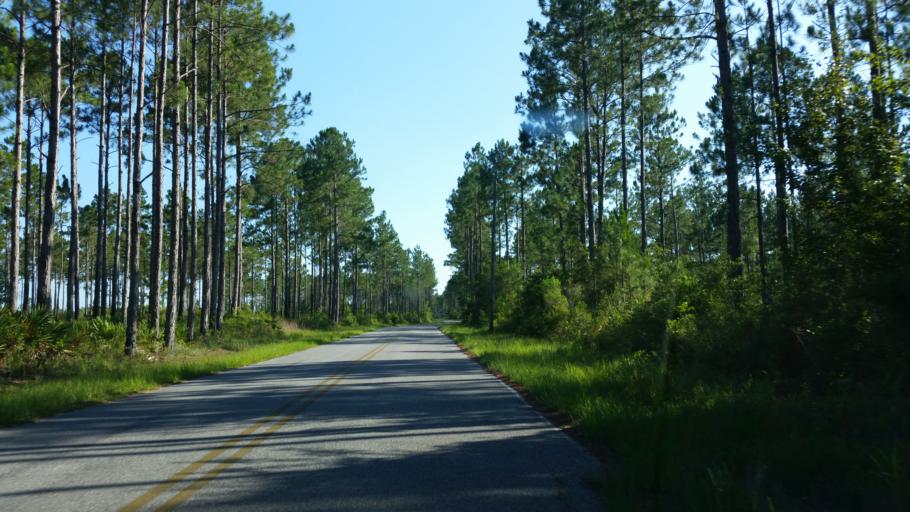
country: US
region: Florida
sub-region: Escambia County
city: Bellview
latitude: 30.4785
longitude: -87.3946
